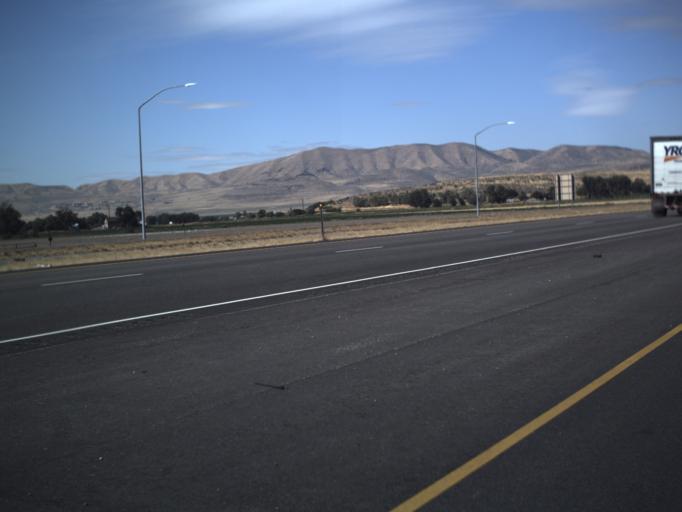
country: US
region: Utah
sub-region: Box Elder County
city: Tremonton
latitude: 41.7124
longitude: -112.2088
